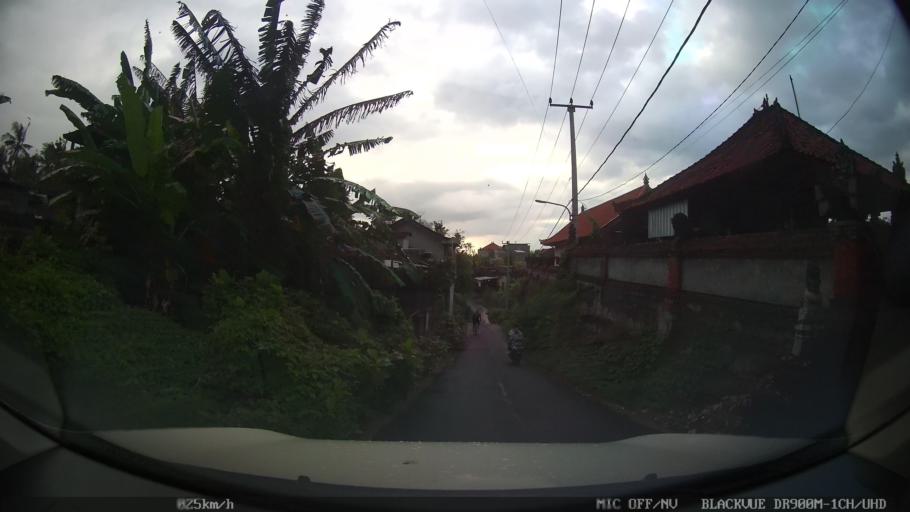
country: ID
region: Bali
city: Banjar Pasekan
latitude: -8.6254
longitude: 115.2763
